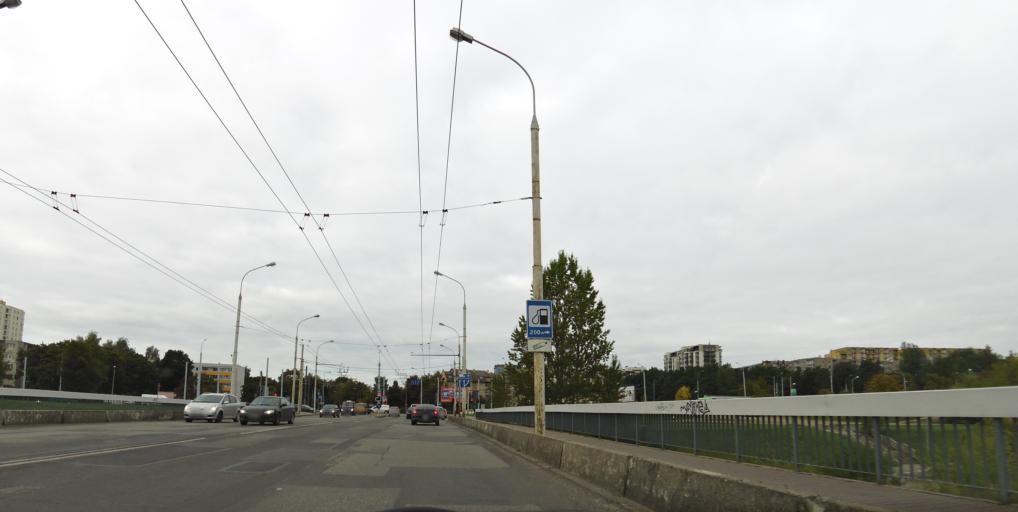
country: LT
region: Vilnius County
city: Rasos
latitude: 54.7056
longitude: 25.3063
